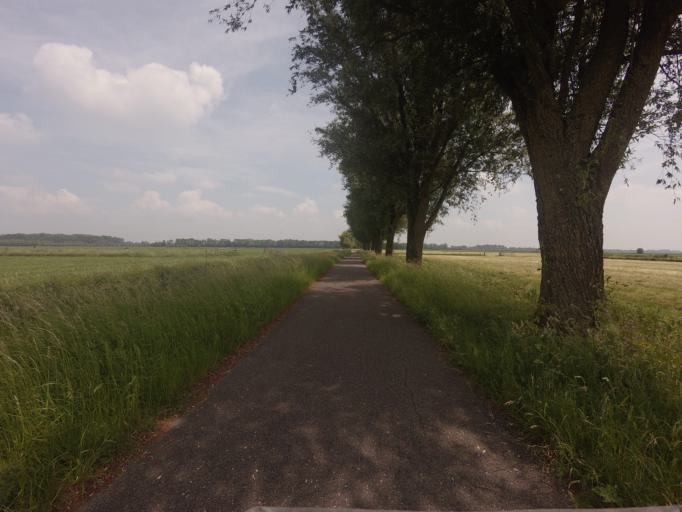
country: NL
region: Utrecht
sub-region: Gemeente Houten
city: Houten
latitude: 51.9938
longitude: 5.1997
